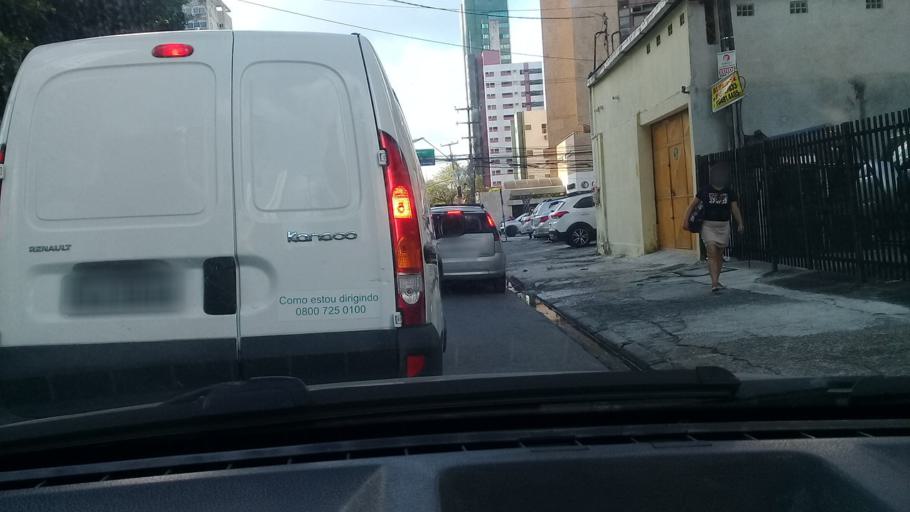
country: BR
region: Pernambuco
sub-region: Recife
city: Recife
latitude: -8.1235
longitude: -34.9059
